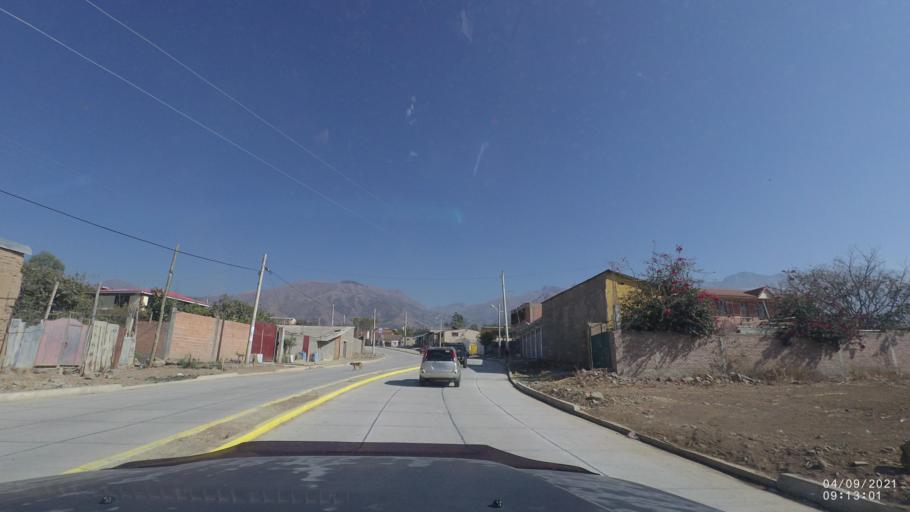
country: BO
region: Cochabamba
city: Sipe Sipe
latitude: -17.3833
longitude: -66.3410
